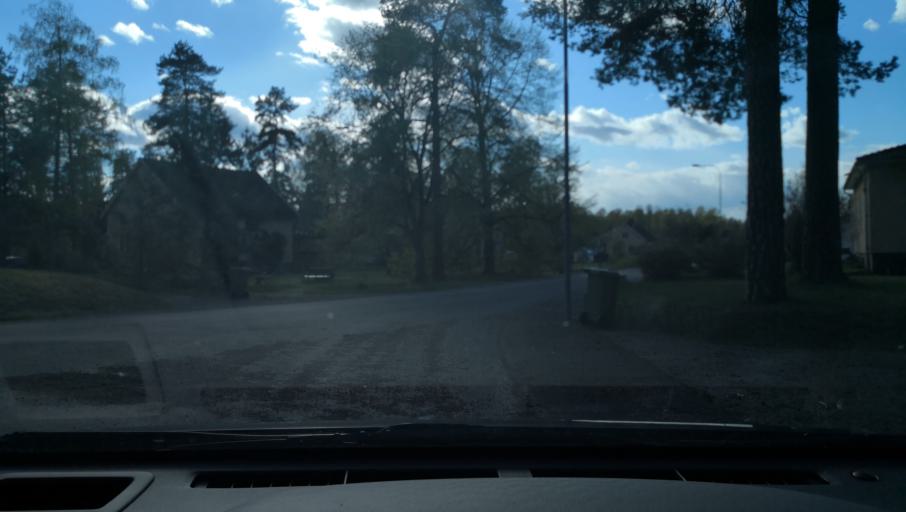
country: SE
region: OErebro
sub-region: Askersunds Kommun
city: Asbro
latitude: 58.9186
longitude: 15.0606
